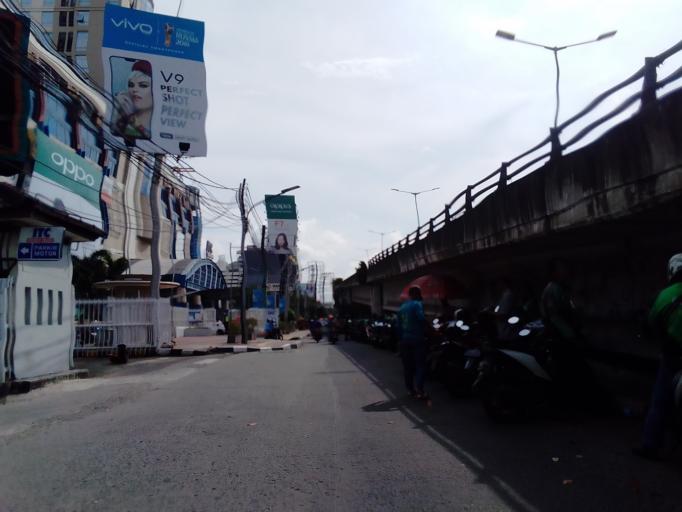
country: ID
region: Jakarta Raya
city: Jakarta
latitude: -6.1661
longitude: 106.8037
